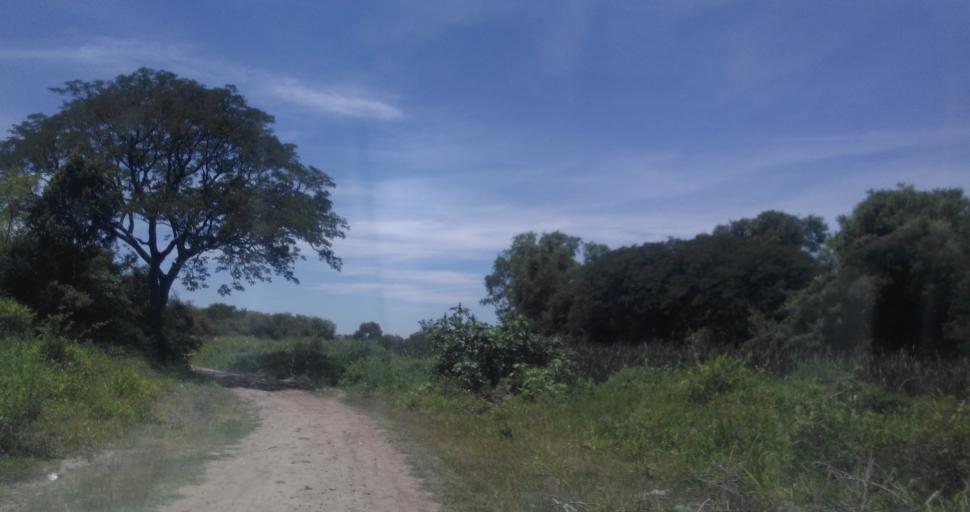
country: AR
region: Chaco
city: Fontana
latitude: -27.4266
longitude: -59.0470
